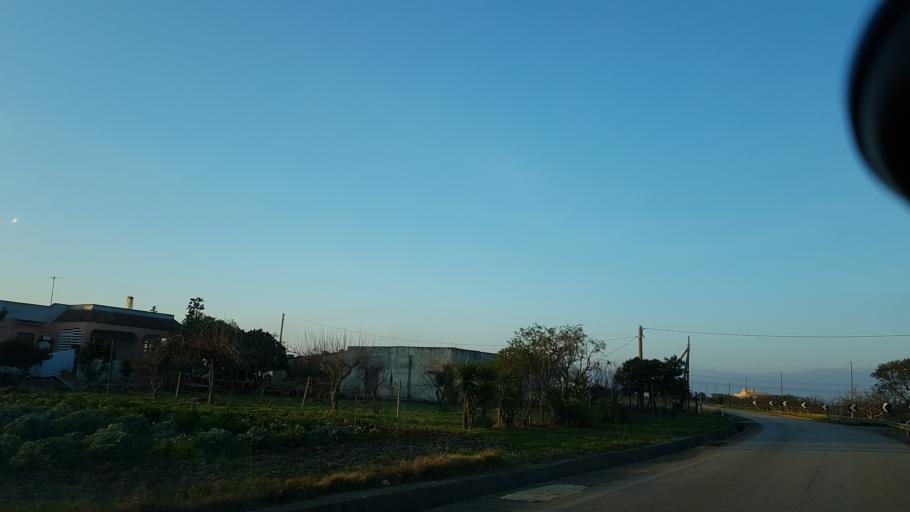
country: IT
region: Apulia
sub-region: Provincia di Brindisi
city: La Rosa
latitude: 40.5964
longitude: 17.9465
